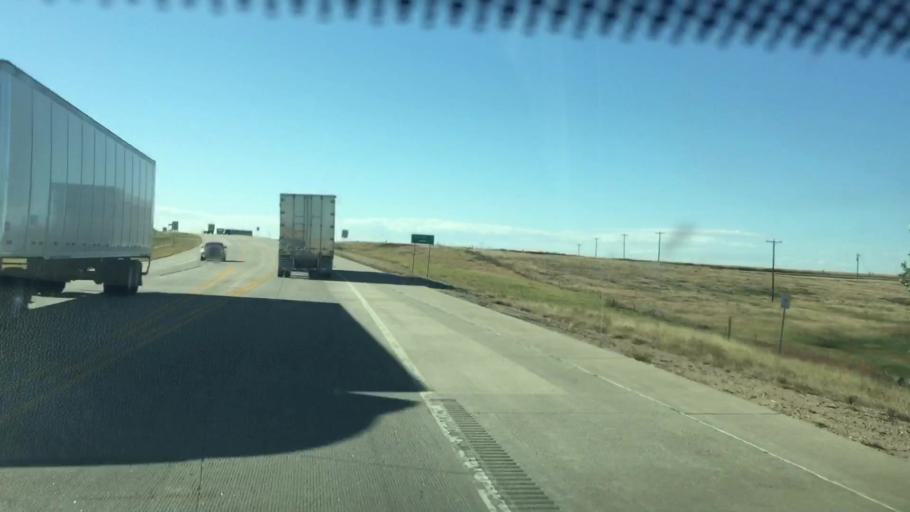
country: US
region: Colorado
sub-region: Kiowa County
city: Eads
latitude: 38.8246
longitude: -102.9947
